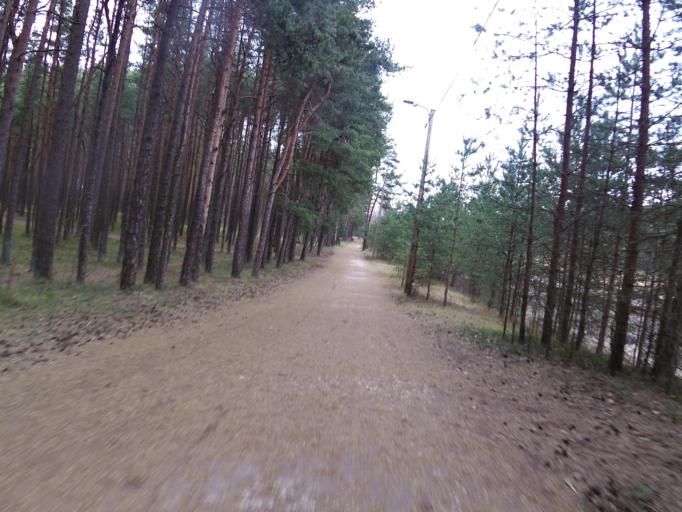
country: EE
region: Harju
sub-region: Tallinna linn
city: Tallinn
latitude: 59.3977
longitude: 24.7310
